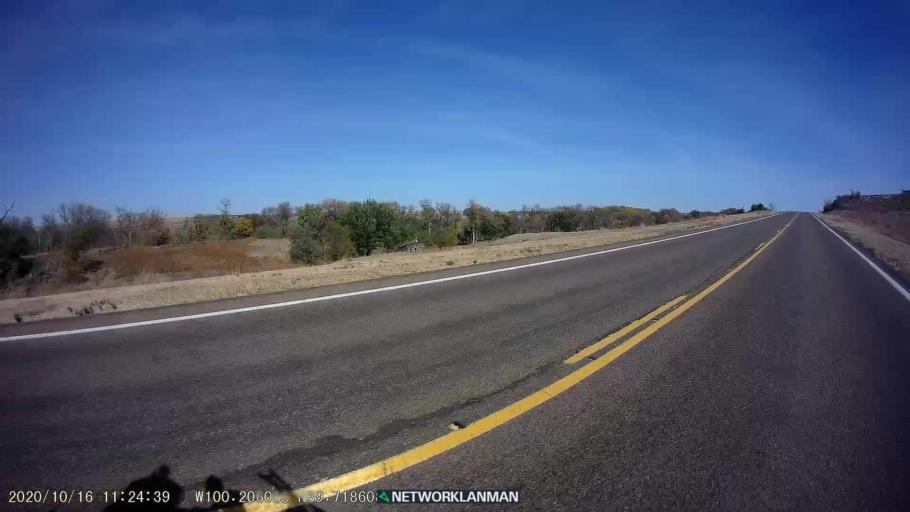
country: US
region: Kansas
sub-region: Norton County
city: Norton
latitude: 39.7188
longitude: -100.2054
